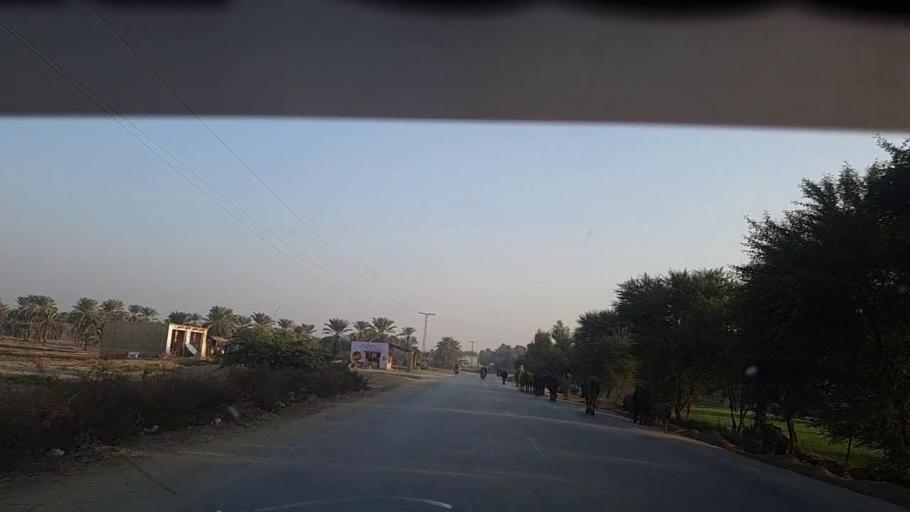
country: PK
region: Sindh
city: Ranipur
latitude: 27.2632
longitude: 68.5240
